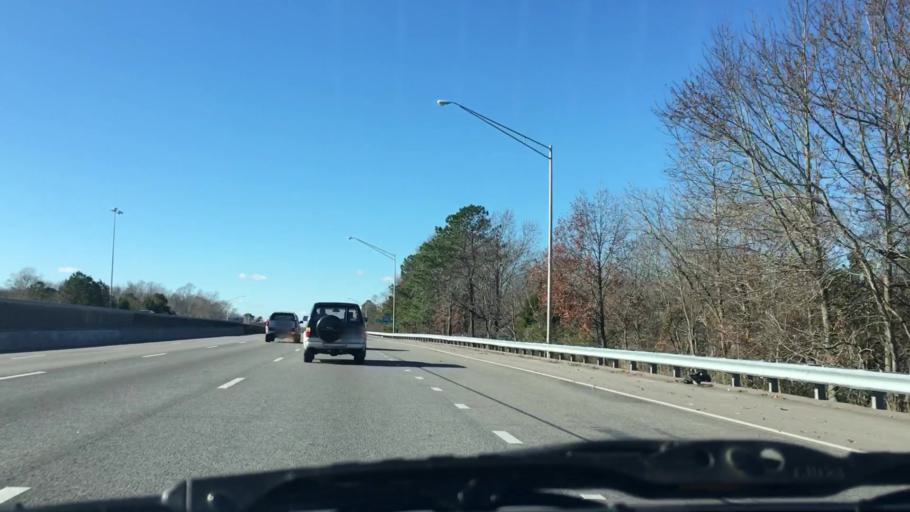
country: US
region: Virginia
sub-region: City of Virginia Beach
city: Virginia Beach
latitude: 36.8442
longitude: -76.0276
